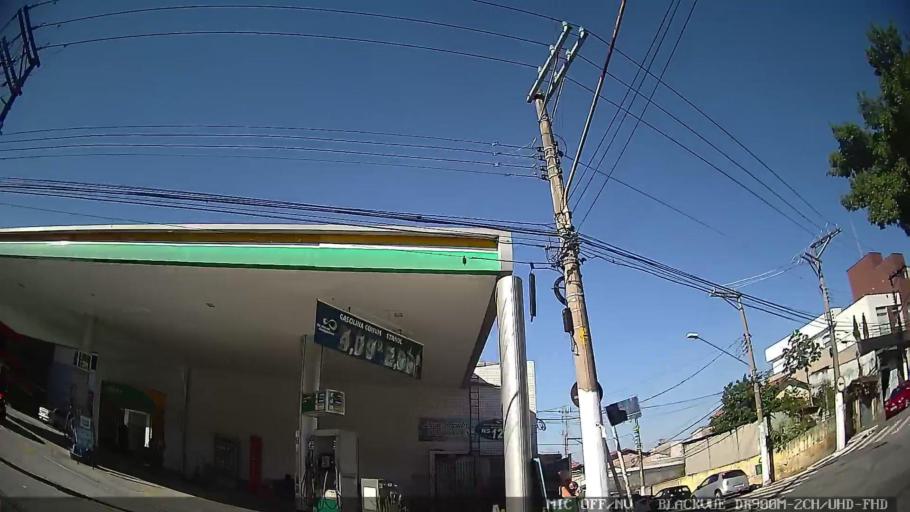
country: BR
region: Sao Paulo
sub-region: Guarulhos
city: Guarulhos
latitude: -23.5460
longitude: -46.5129
